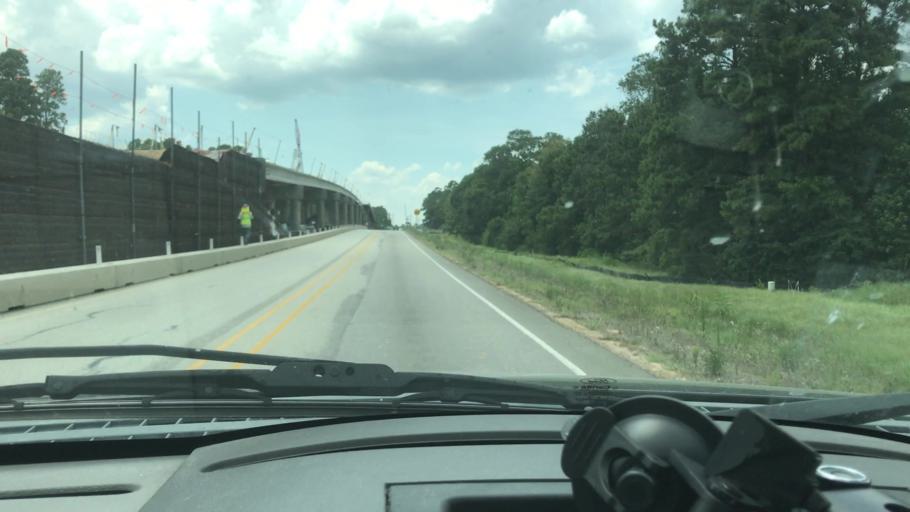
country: US
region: Texas
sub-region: Montgomery County
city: Conroe
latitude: 30.3498
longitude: -95.4561
